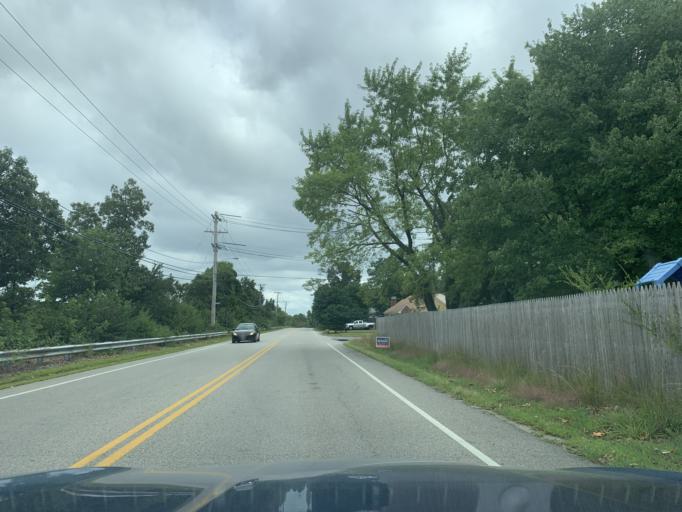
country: US
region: Rhode Island
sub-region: Kent County
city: Warwick
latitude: 41.7230
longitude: -71.4651
